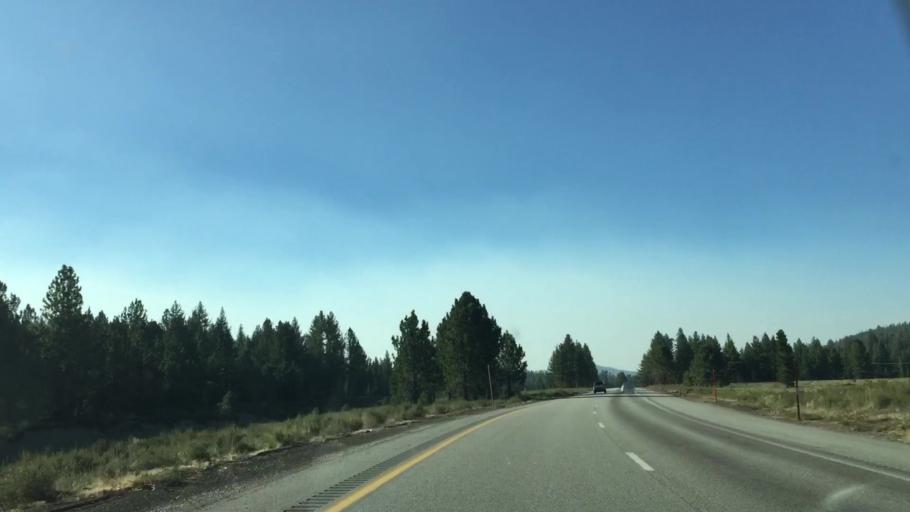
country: US
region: California
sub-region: Mono County
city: Mammoth Lakes
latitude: 37.6966
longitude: -118.9480
